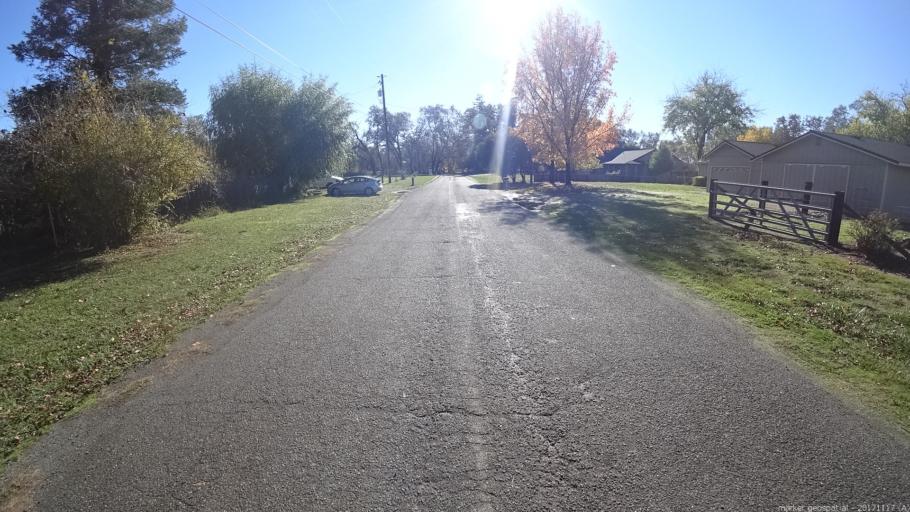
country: US
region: California
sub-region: Shasta County
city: Cottonwood
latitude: 40.4271
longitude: -122.2172
